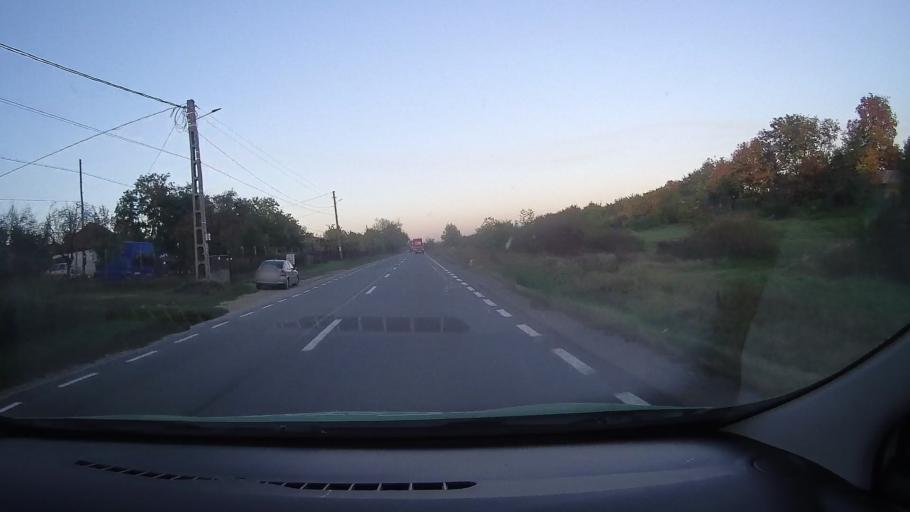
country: RO
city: Szekelyhid
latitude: 47.3621
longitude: 22.1150
